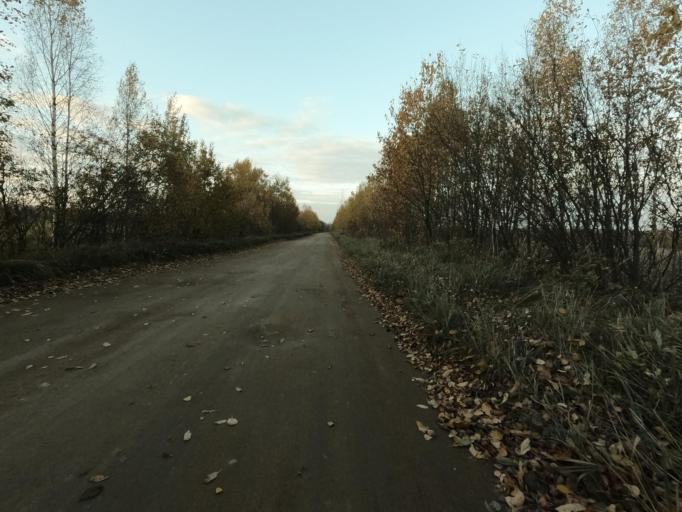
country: RU
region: Leningrad
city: Mga
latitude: 59.8013
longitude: 31.2005
